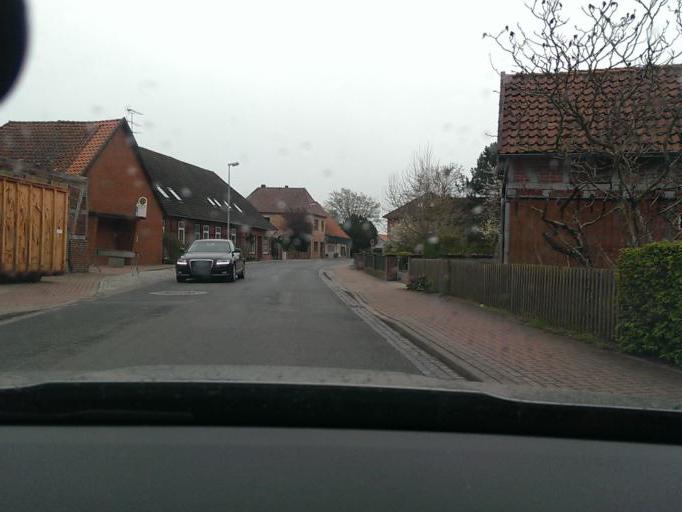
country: DE
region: Lower Saxony
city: Steimbke
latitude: 52.6558
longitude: 9.4848
